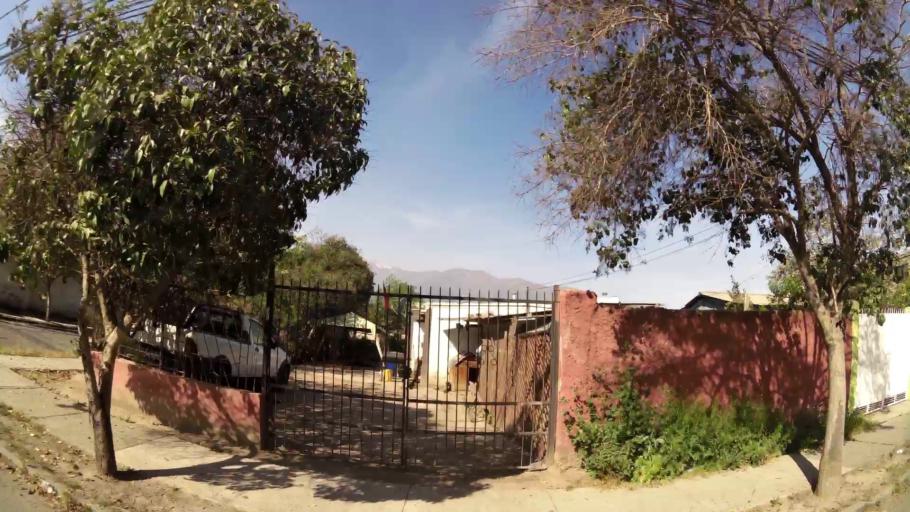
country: CL
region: Santiago Metropolitan
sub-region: Provincia de Santiago
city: La Pintana
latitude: -33.5312
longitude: -70.5914
